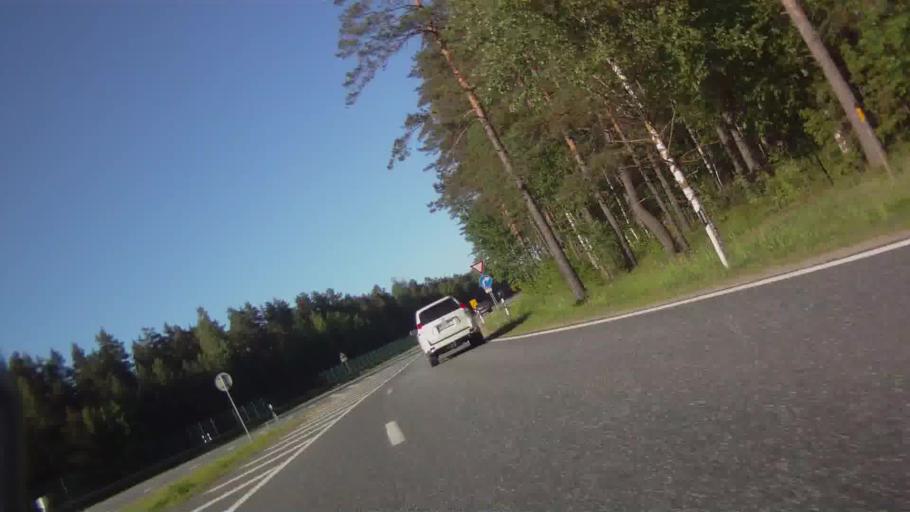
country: LV
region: Riga
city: Bergi
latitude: 57.0115
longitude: 24.3137
